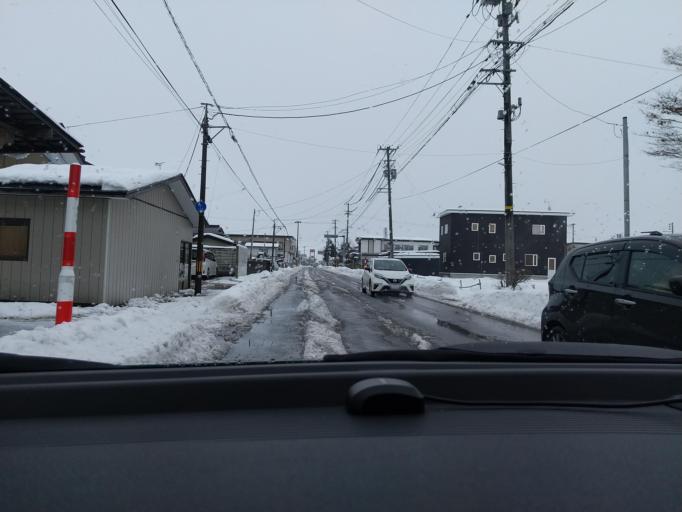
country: JP
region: Akita
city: Omagari
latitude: 39.4497
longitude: 140.4786
